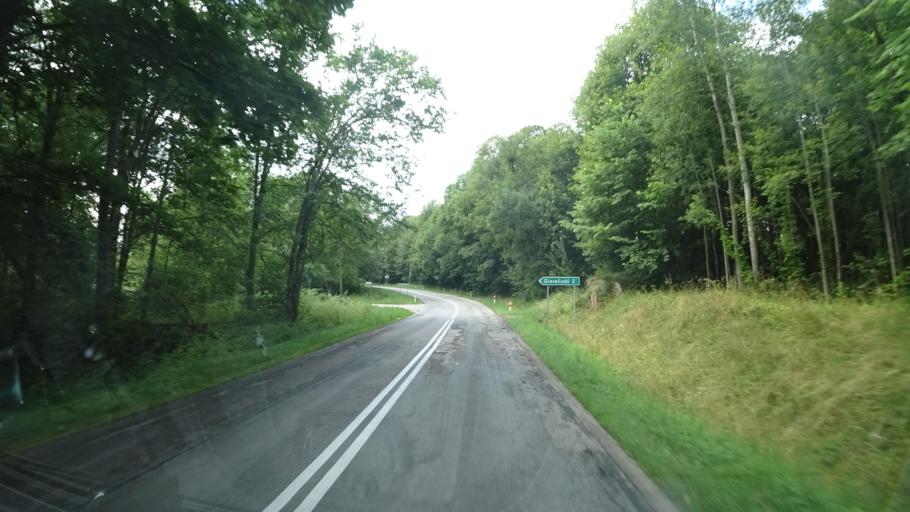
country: PL
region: Warmian-Masurian Voivodeship
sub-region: Powiat goldapski
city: Goldap
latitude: 54.2110
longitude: 22.2081
